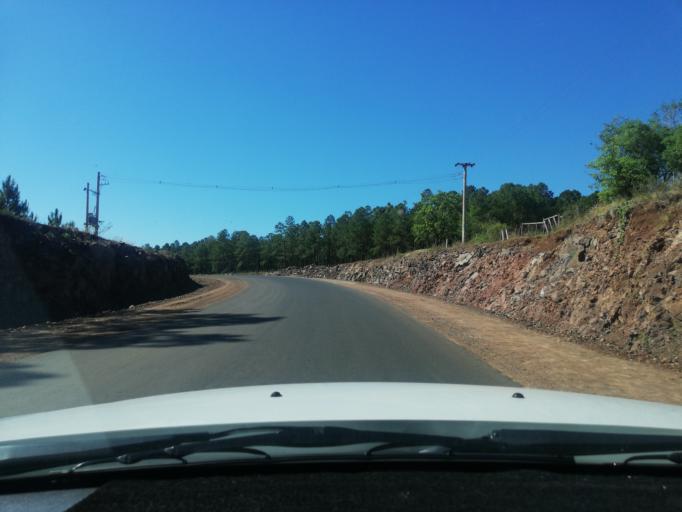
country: AR
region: Misiones
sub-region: Departamento de Candelaria
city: Candelaria
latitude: -27.5102
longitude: -55.7363
